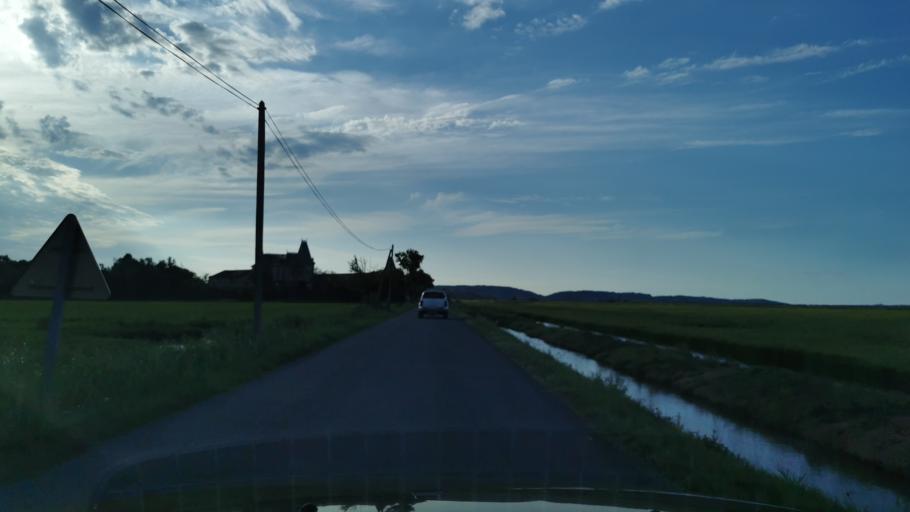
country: FR
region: Languedoc-Roussillon
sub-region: Departement de l'Aude
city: Gruissan
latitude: 43.1215
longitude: 3.0325
